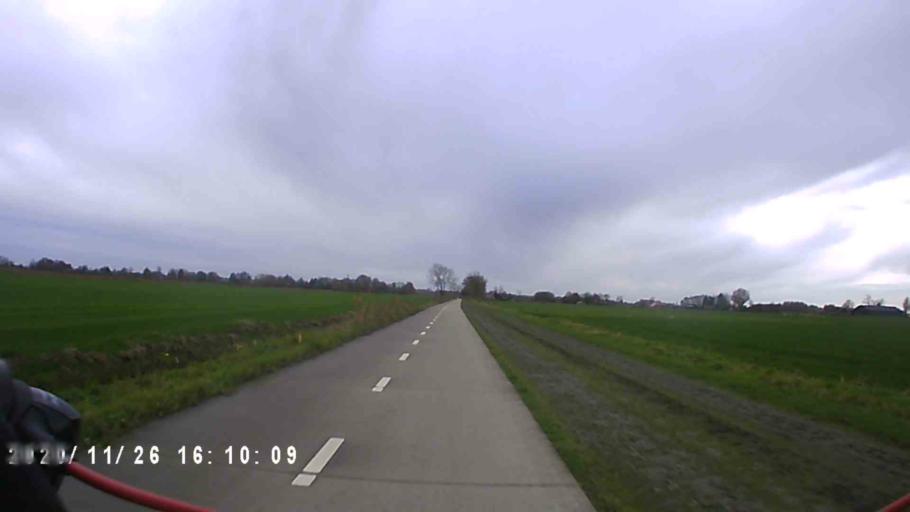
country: NL
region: Groningen
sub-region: Gemeente Bedum
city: Bedum
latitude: 53.2549
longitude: 6.6548
